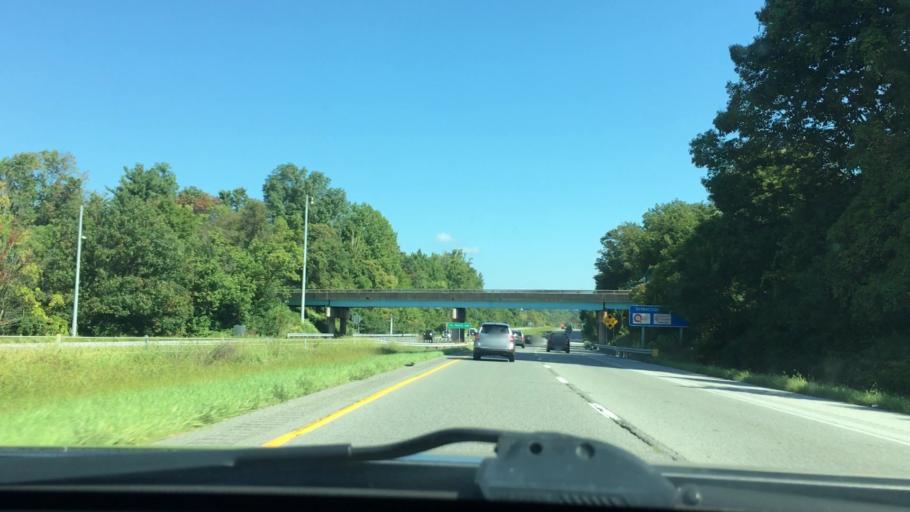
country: US
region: Pennsylvania
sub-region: Chester County
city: West Chester
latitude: 39.9909
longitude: -75.5889
